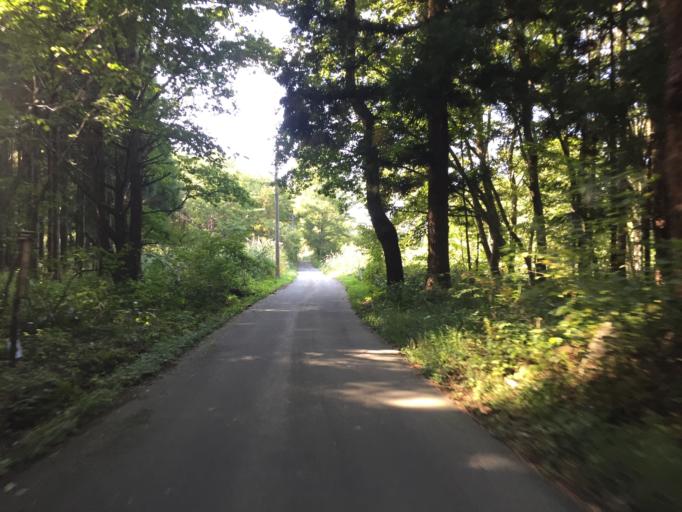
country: JP
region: Yamagata
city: Yonezawa
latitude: 37.8315
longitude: 140.2101
